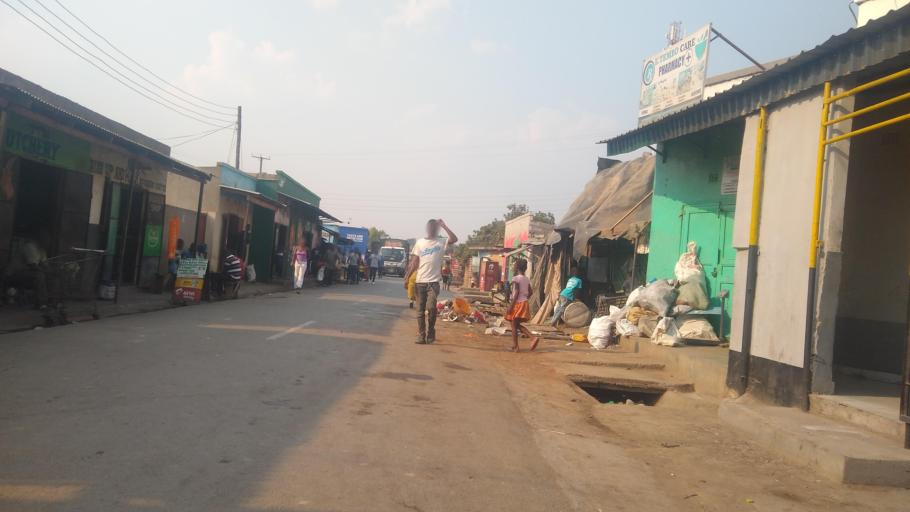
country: ZM
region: Lusaka
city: Lusaka
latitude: -15.4441
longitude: 28.3802
